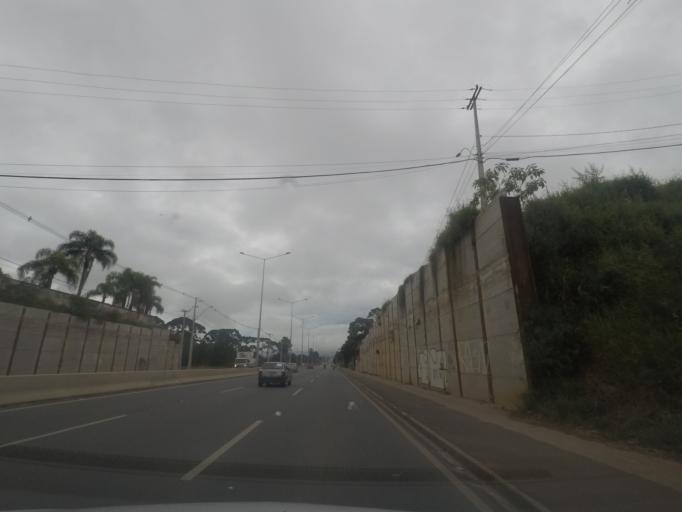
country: BR
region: Parana
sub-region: Piraquara
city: Piraquara
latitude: -25.4565
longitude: -49.1057
